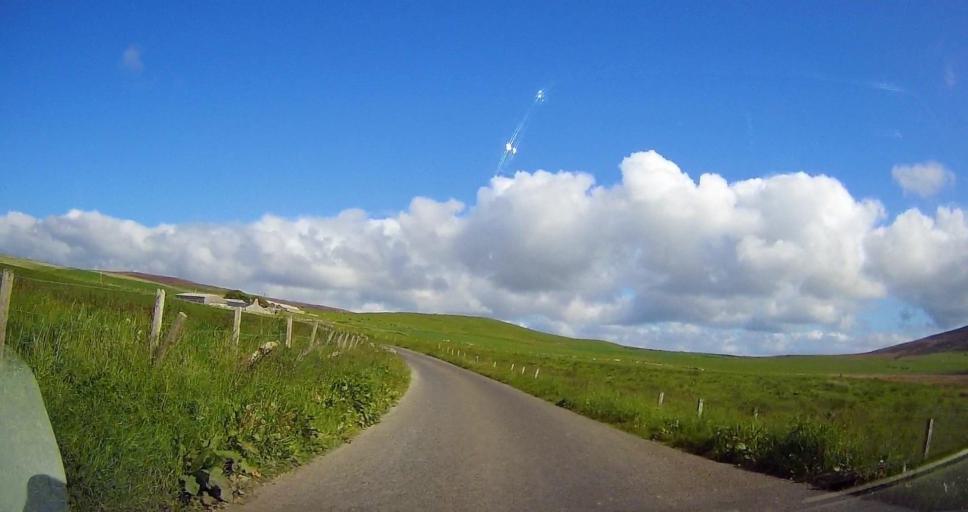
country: GB
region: Scotland
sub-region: Orkney Islands
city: Stromness
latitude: 58.9838
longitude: -3.1466
